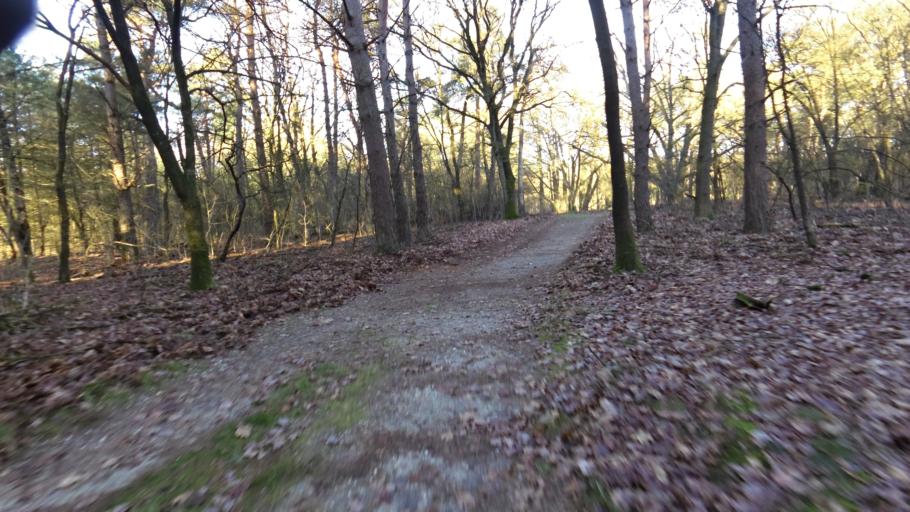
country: NL
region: Gelderland
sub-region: Gemeente Barneveld
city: Garderen
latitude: 52.2138
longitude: 5.7181
